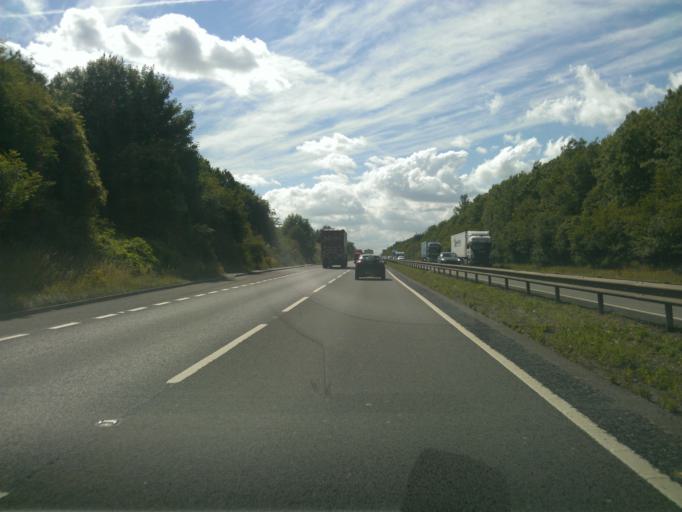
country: GB
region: England
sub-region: Northamptonshire
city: Finedon
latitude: 52.3820
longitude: -0.6338
